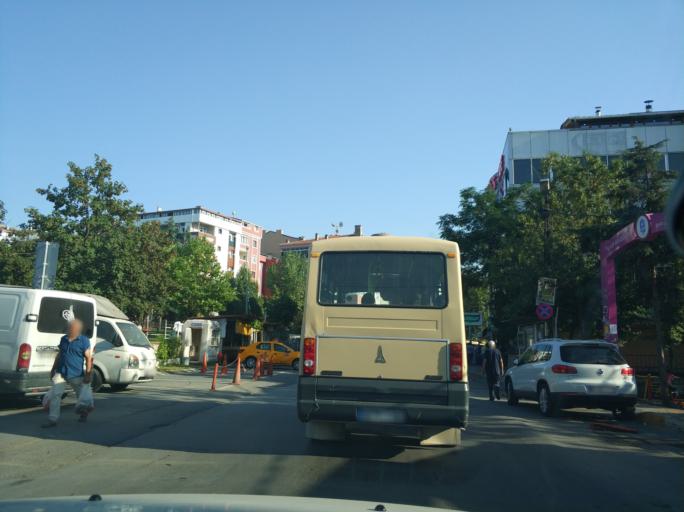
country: TR
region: Istanbul
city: Sultangazi
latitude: 41.0813
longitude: 28.9202
